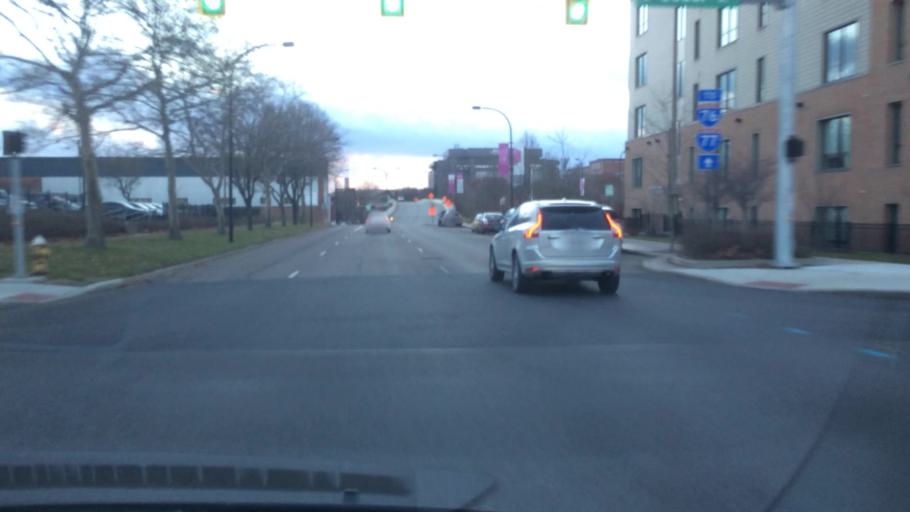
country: US
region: Ohio
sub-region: Summit County
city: Akron
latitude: 41.0750
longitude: -81.5216
